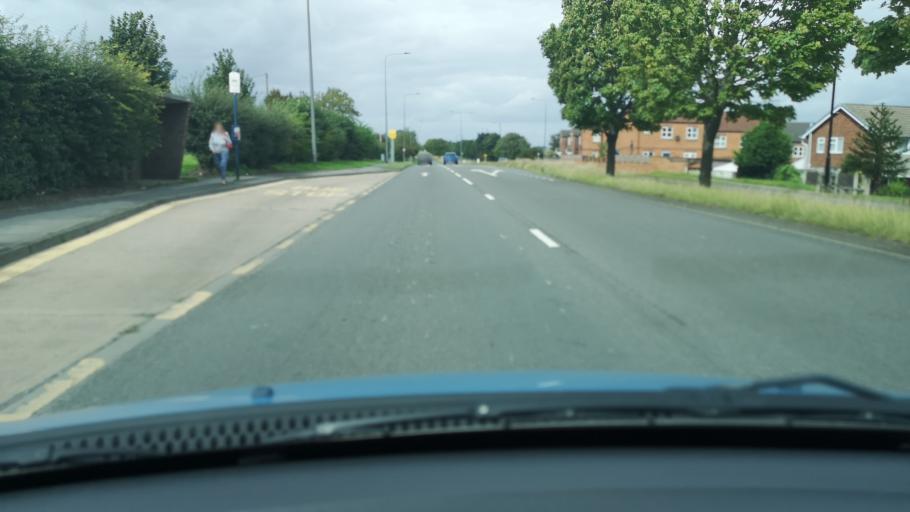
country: GB
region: England
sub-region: Doncaster
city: Carcroft
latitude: 53.5696
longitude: -1.1995
